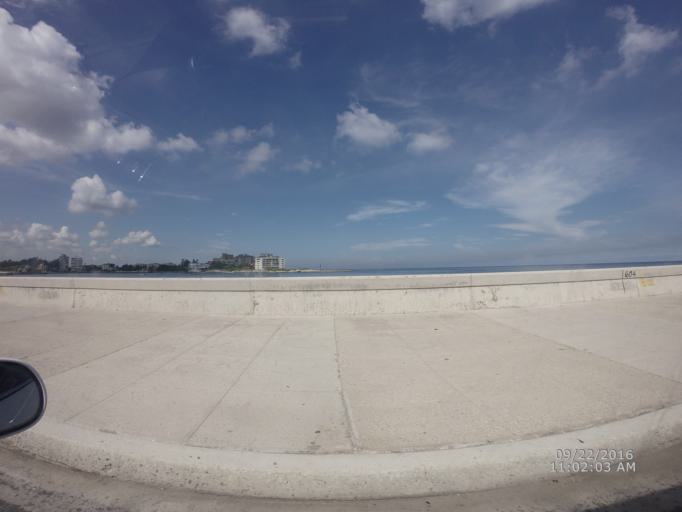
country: CU
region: La Habana
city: Havana
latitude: 23.1340
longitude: -82.4081
